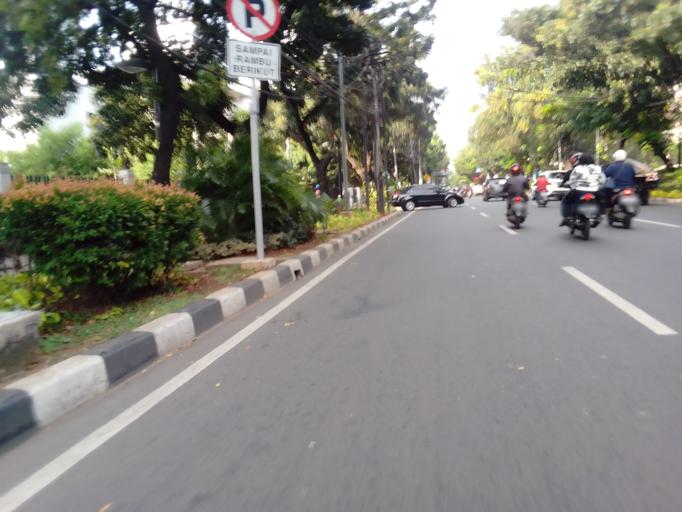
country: ID
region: Jakarta Raya
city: Jakarta
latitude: -6.1831
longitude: 106.8257
